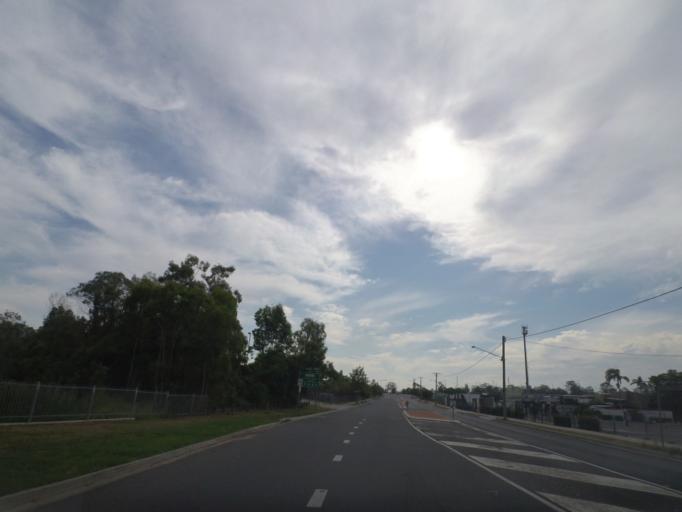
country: AU
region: Queensland
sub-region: Brisbane
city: Richlands
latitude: -27.5935
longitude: 152.9516
